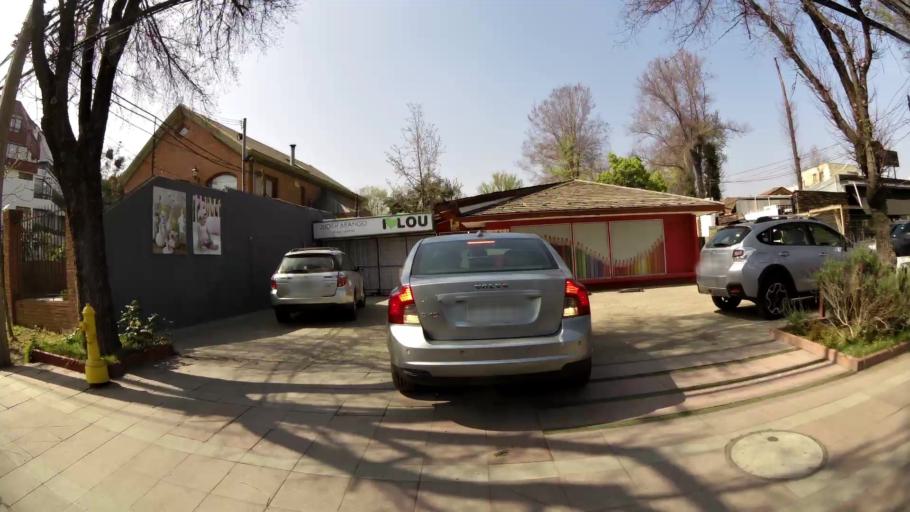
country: CL
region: Santiago Metropolitan
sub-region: Provincia de Santiago
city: Villa Presidente Frei, Nunoa, Santiago, Chile
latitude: -33.3862
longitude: -70.5755
